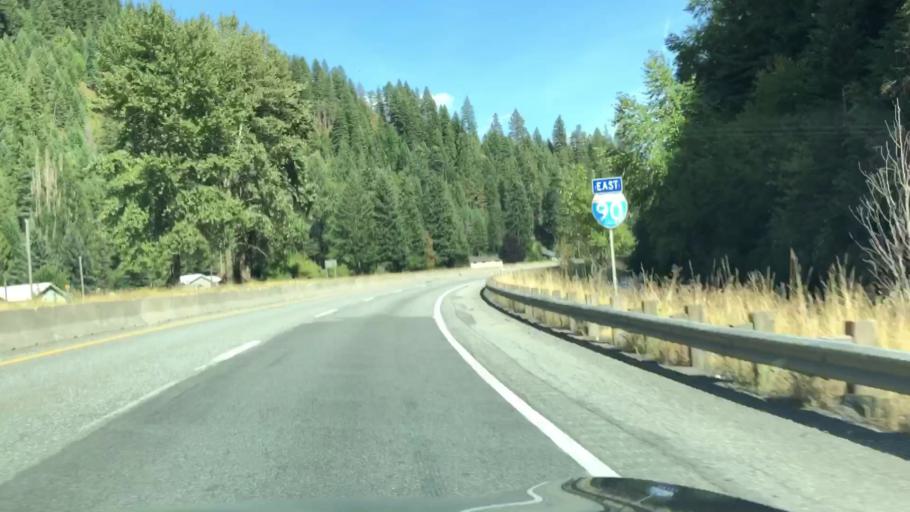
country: US
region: Idaho
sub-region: Shoshone County
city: Wallace
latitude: 47.4745
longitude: -115.9072
